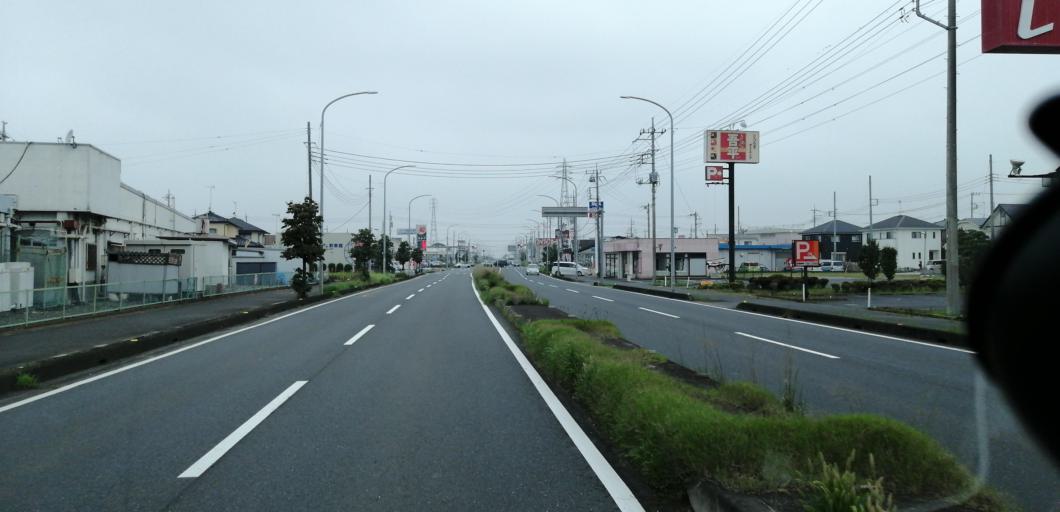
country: JP
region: Saitama
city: Kazo
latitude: 36.1322
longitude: 139.6036
